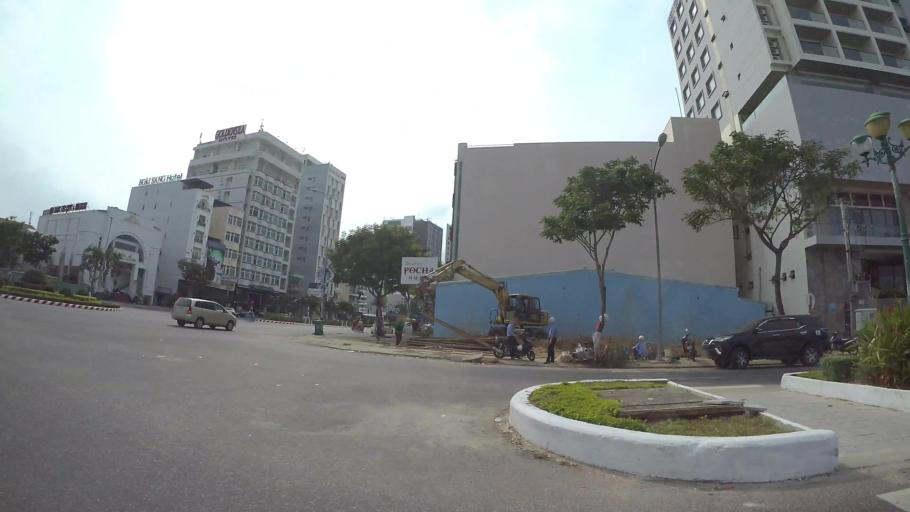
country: VN
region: Da Nang
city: Son Tra
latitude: 16.0706
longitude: 108.2382
